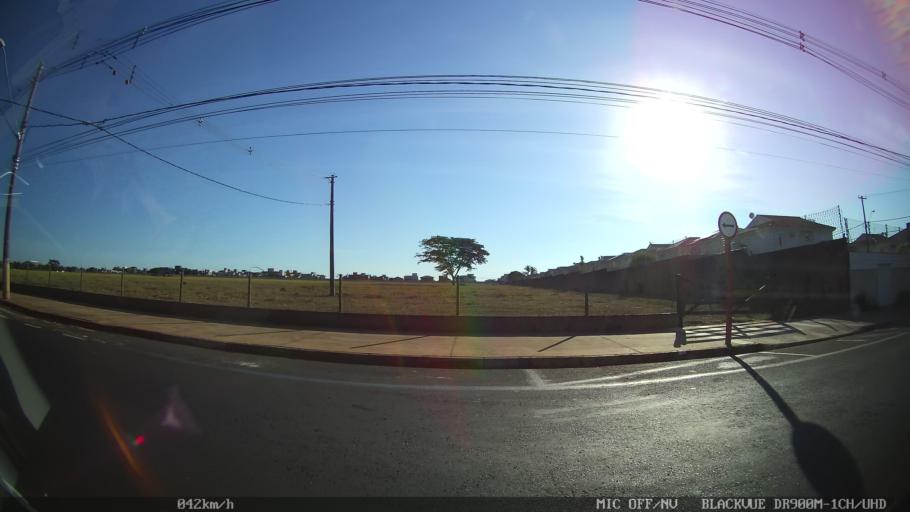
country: BR
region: Sao Paulo
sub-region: Sao Jose Do Rio Preto
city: Sao Jose do Rio Preto
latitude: -20.8499
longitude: -49.4133
